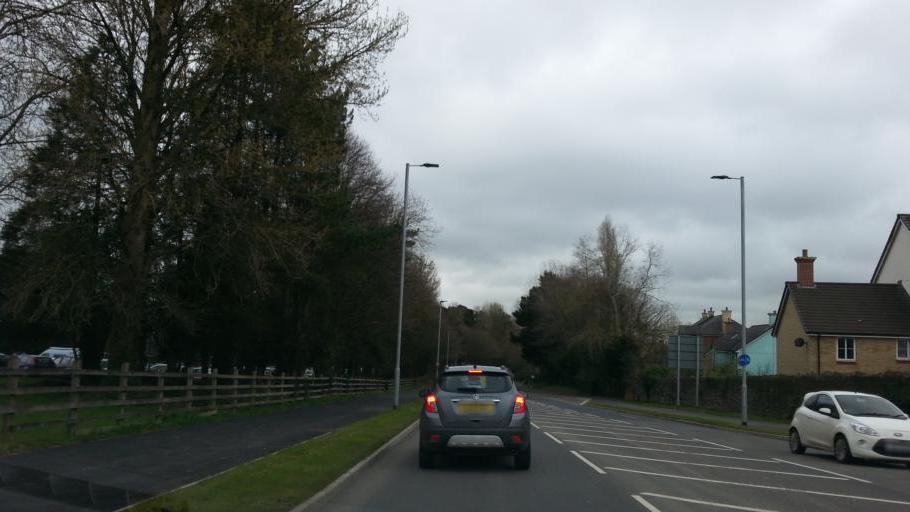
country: GB
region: England
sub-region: Devon
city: Barnstaple
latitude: 51.0927
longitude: -4.0541
